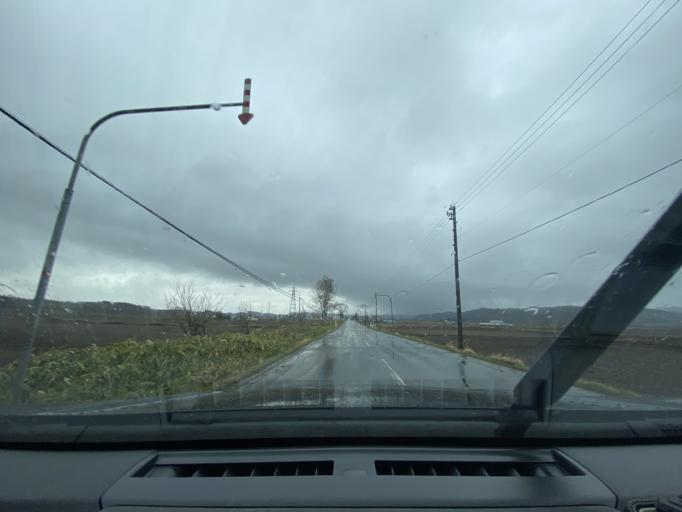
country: JP
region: Hokkaido
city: Fukagawa
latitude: 43.8320
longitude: 141.8971
